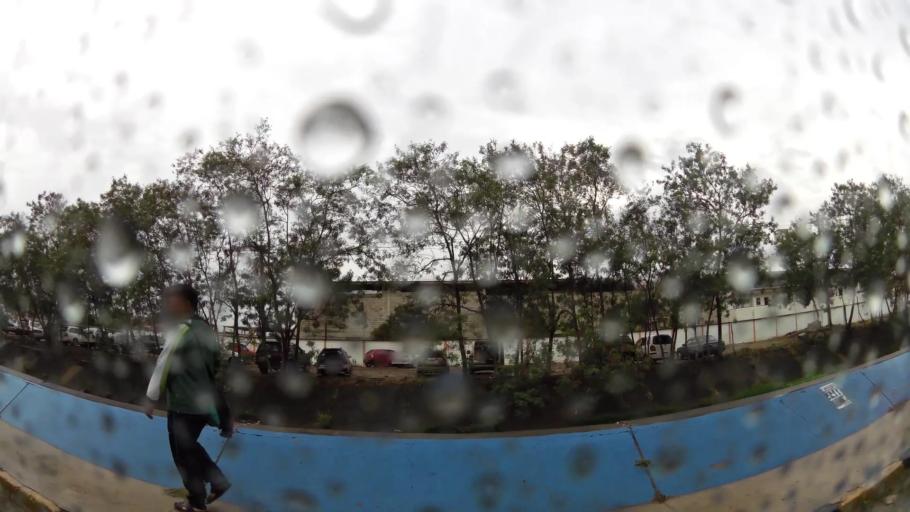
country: BO
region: Santa Cruz
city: Santa Cruz de la Sierra
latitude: -17.7752
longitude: -63.1427
